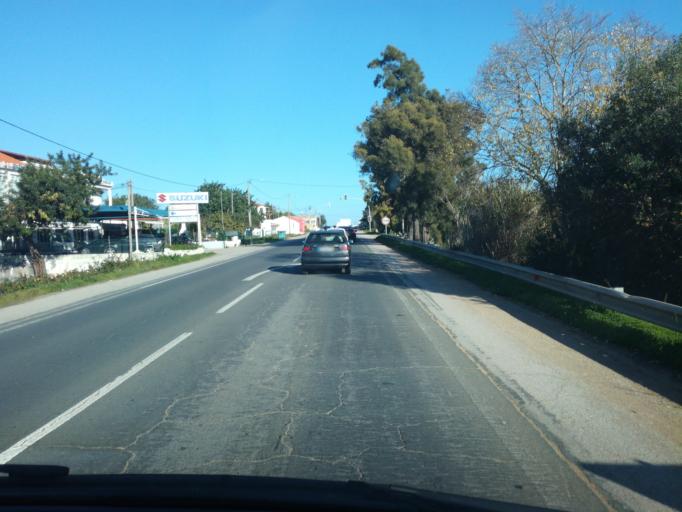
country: PT
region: Faro
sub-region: Olhao
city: Laranjeiro
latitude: 37.0575
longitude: -7.7695
